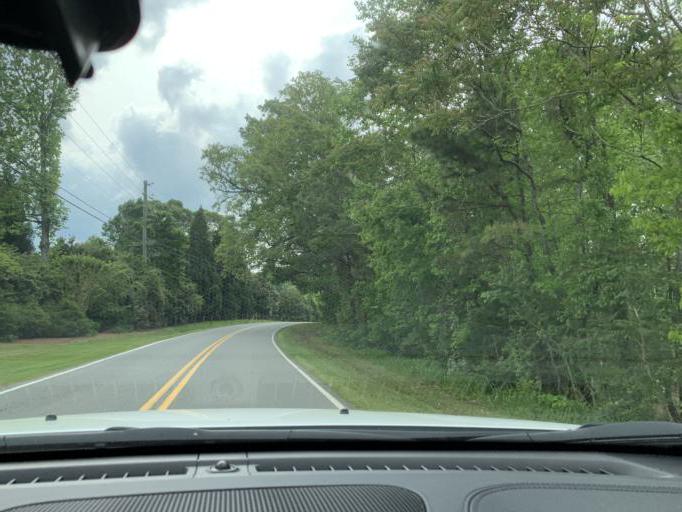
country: US
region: Georgia
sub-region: Gwinnett County
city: Suwanee
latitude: 34.1012
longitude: -84.1212
